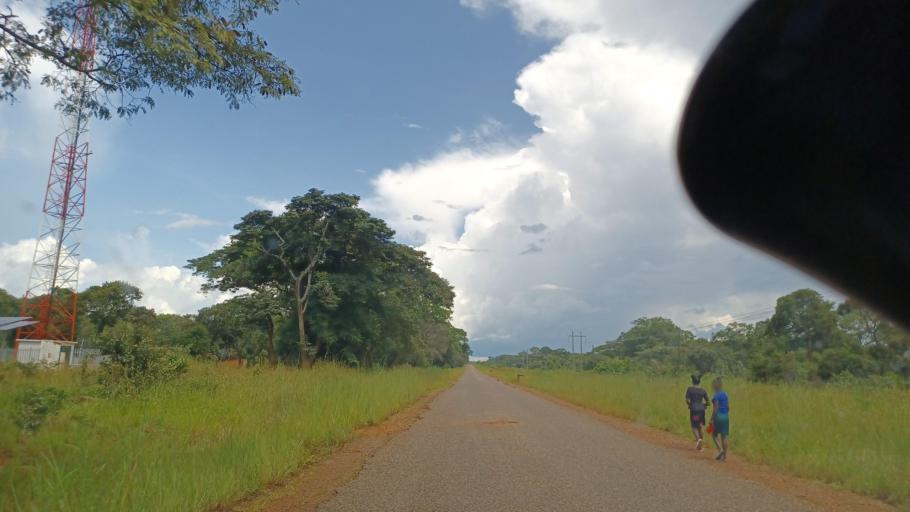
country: ZM
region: North-Western
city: Kasempa
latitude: -12.8902
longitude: 26.0503
